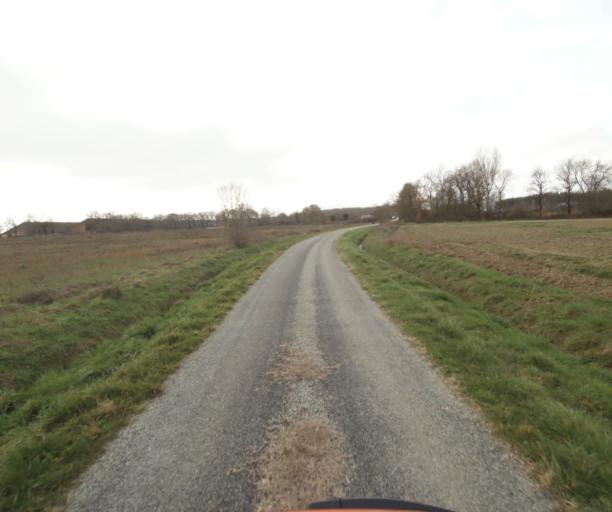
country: FR
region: Midi-Pyrenees
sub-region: Departement de l'Ariege
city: Mazeres
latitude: 43.2009
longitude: 1.6750
